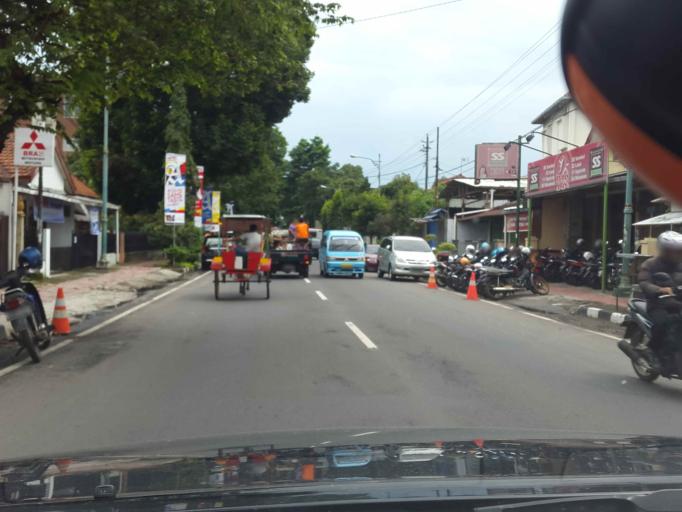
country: ID
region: Central Java
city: Salatiga
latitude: -7.3401
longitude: 110.5088
